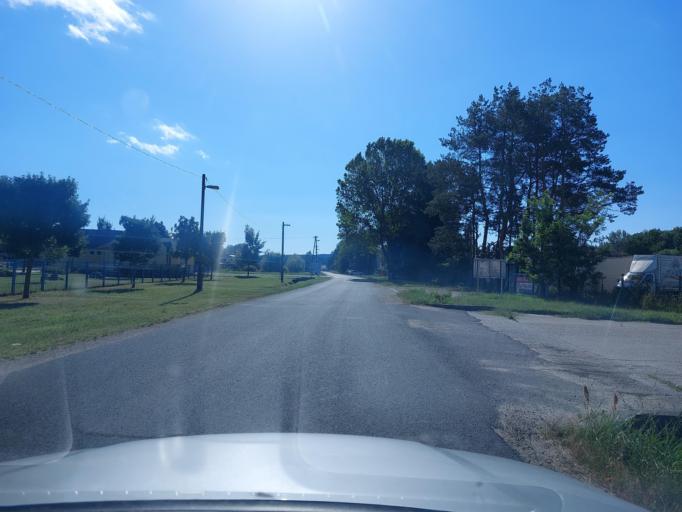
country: HU
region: Veszprem
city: Ajka
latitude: 47.1257
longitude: 17.5394
